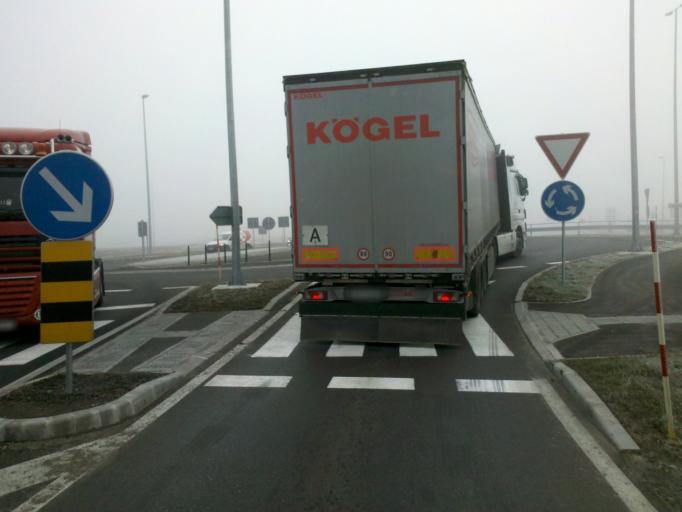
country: HR
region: Varazdinska
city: Varazdin
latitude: 46.2652
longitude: 16.3751
